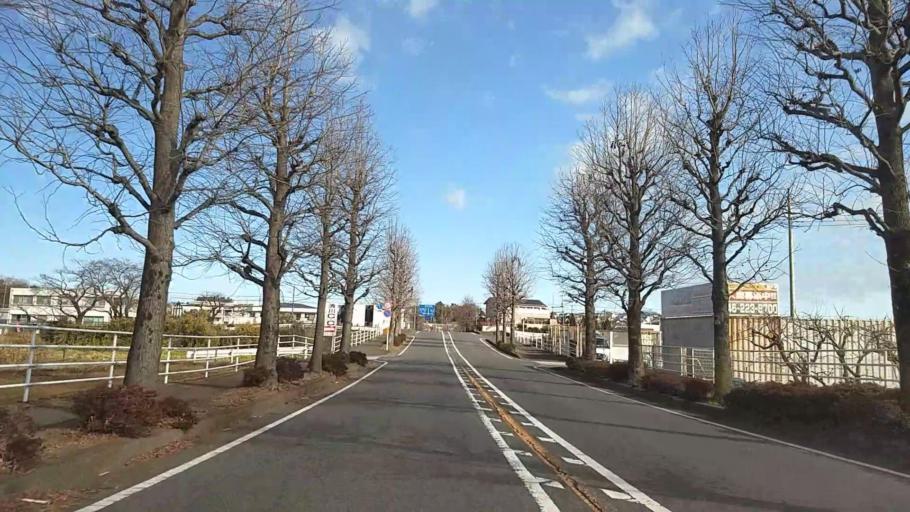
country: JP
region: Kanagawa
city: Atsugi
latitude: 35.4292
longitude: 139.3290
